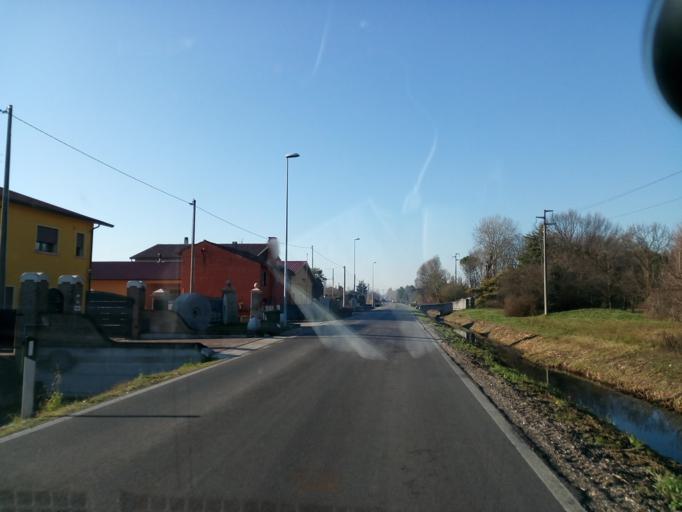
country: IT
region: Veneto
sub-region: Provincia di Venezia
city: Stigliano
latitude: 45.5156
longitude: 12.0480
